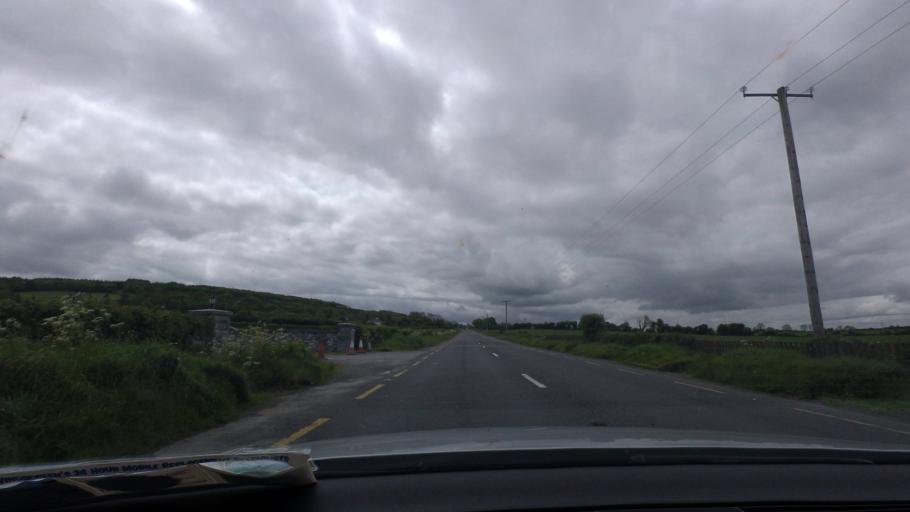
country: IE
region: Munster
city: Cashel
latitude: 52.5411
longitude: -7.8695
